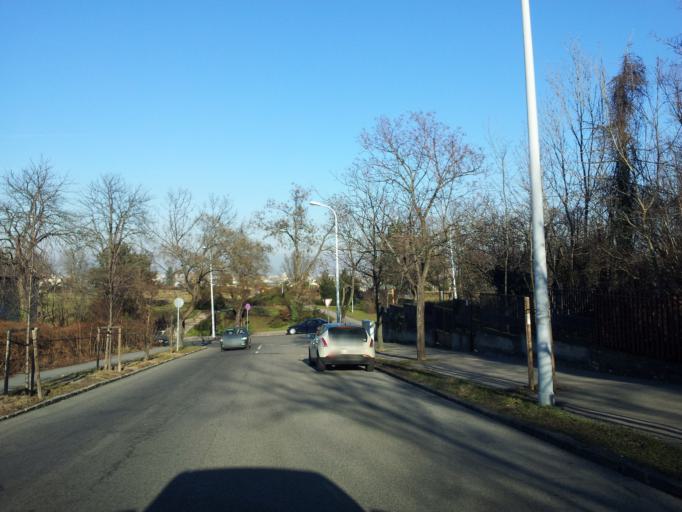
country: HU
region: Budapest
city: Budapest I. keruelet
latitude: 47.4884
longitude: 19.0372
